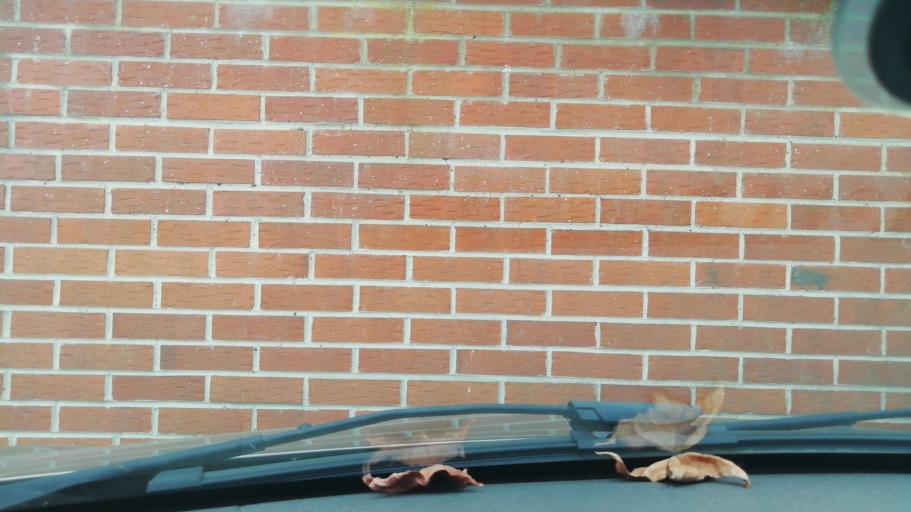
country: FR
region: Nord-Pas-de-Calais
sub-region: Departement du Pas-de-Calais
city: Aubigny-en-Artois
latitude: 50.3238
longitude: 2.5864
